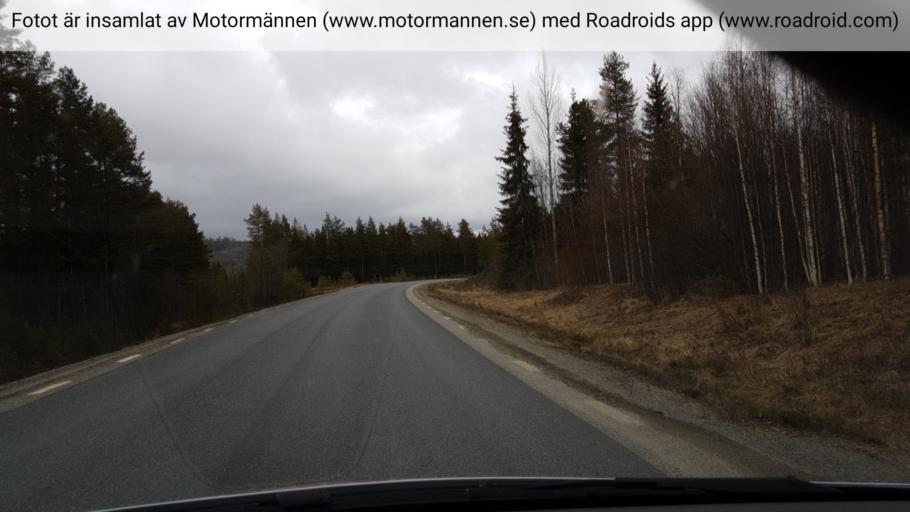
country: SE
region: Vaesternorrland
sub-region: OErnskoeldsviks Kommun
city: Bredbyn
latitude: 63.8791
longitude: 18.5081
